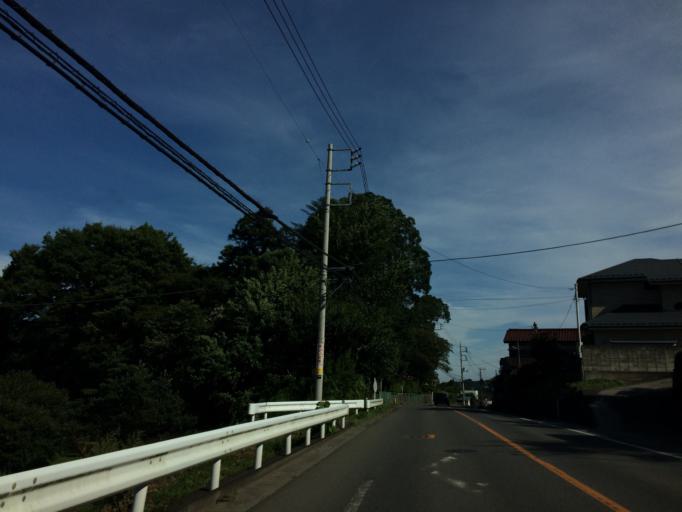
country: JP
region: Gunma
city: Shibukawa
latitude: 36.5416
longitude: 138.9507
